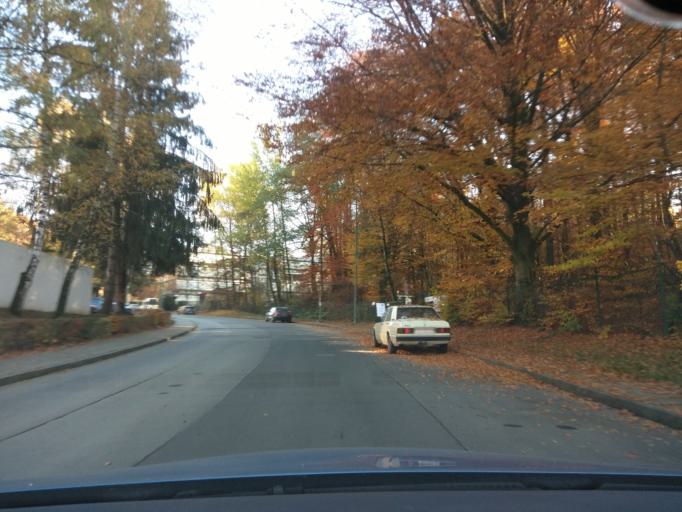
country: DE
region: Bavaria
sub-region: Lower Bavaria
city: Passau
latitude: 48.5609
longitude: 13.4150
